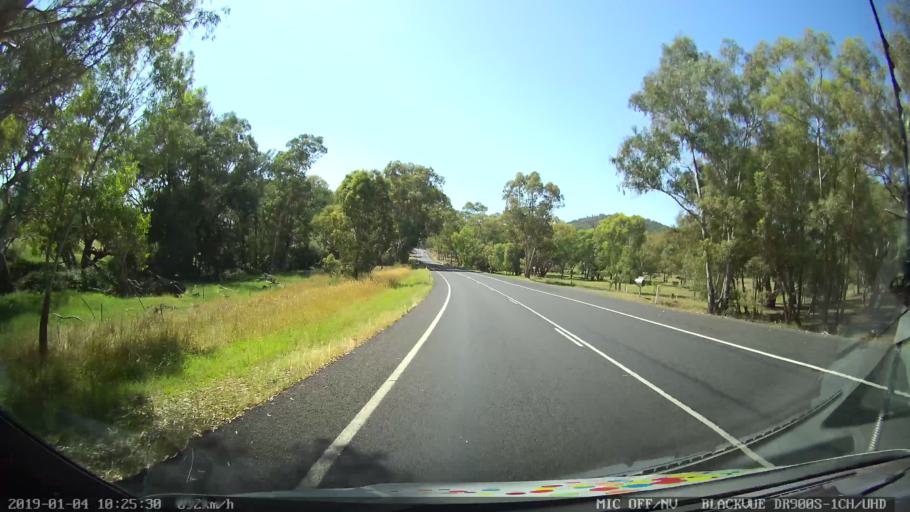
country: AU
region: New South Wales
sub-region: Cabonne
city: Canowindra
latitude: -33.3697
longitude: 148.5708
